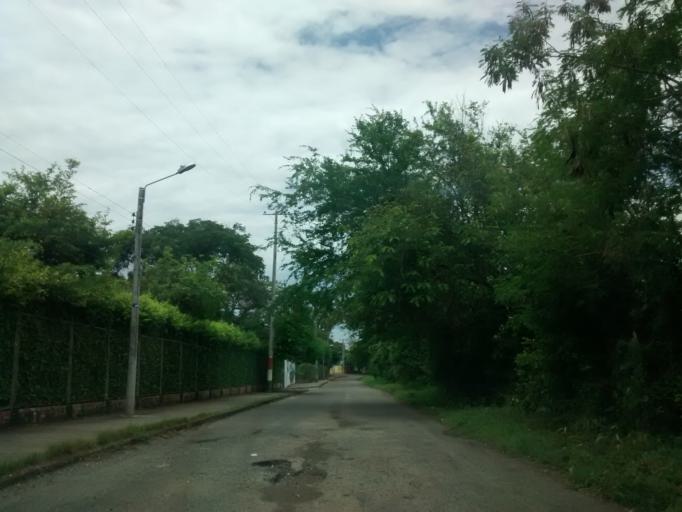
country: CO
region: Cundinamarca
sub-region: Girardot
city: Girardot City
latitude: 4.3076
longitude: -74.8103
